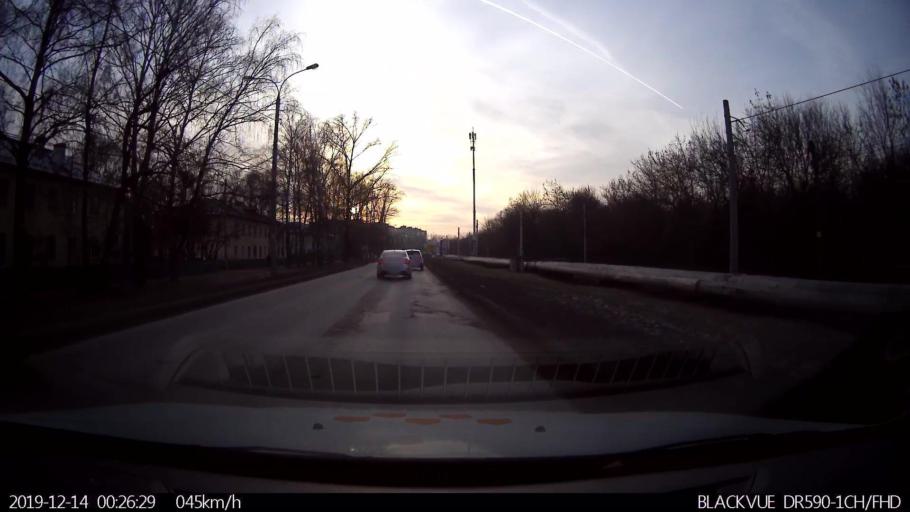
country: RU
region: Nizjnij Novgorod
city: Burevestnik
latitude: 56.2257
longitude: 43.8378
